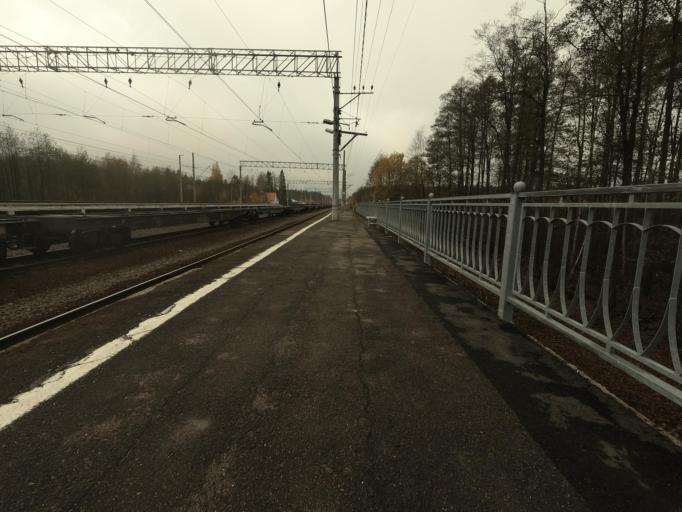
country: RU
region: Leningrad
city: Pavlovo
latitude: 59.7920
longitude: 30.8805
